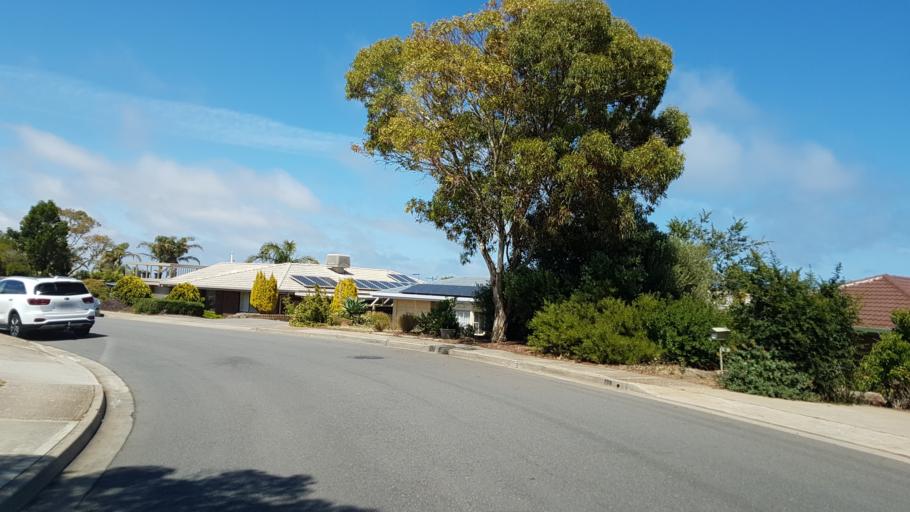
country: AU
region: South Australia
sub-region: Marion
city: Marino
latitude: -35.0675
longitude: 138.5099
